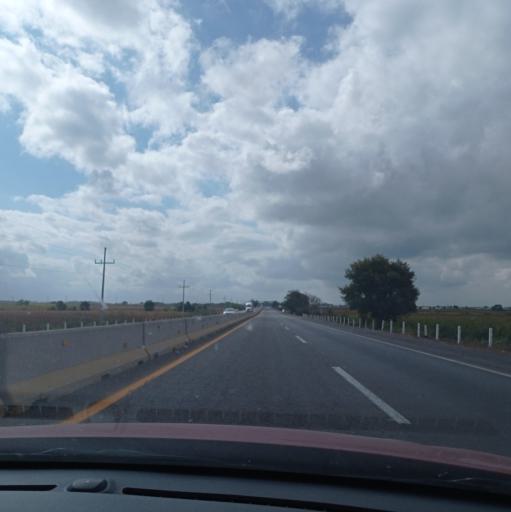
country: MX
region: Sinaloa
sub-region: Navolato
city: General Angel Flores (La Palma)
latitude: 24.8320
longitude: -107.5973
